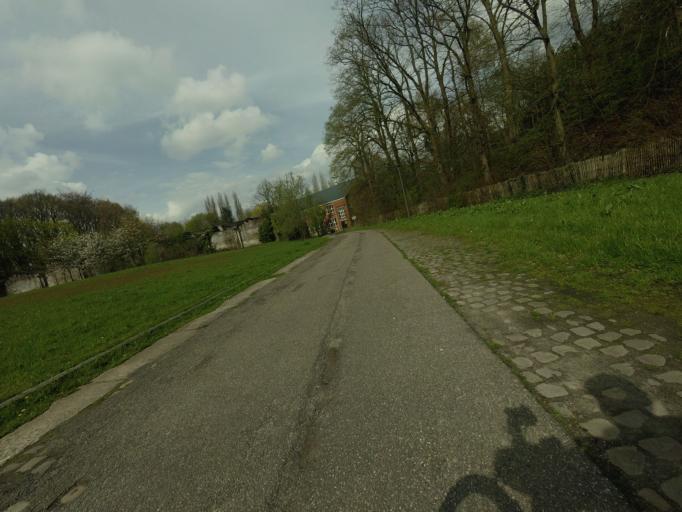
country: BE
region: Flanders
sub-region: Provincie Antwerpen
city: Mortsel
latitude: 51.1736
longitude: 4.4622
